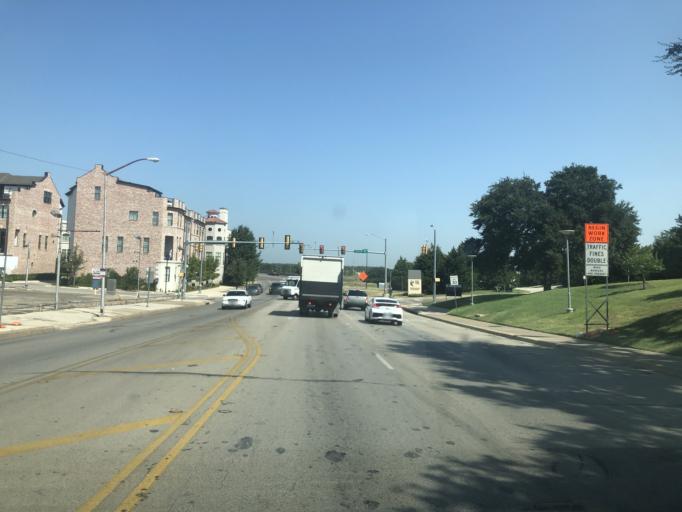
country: US
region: Texas
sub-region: Tarrant County
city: Fort Worth
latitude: 32.7556
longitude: -97.3398
